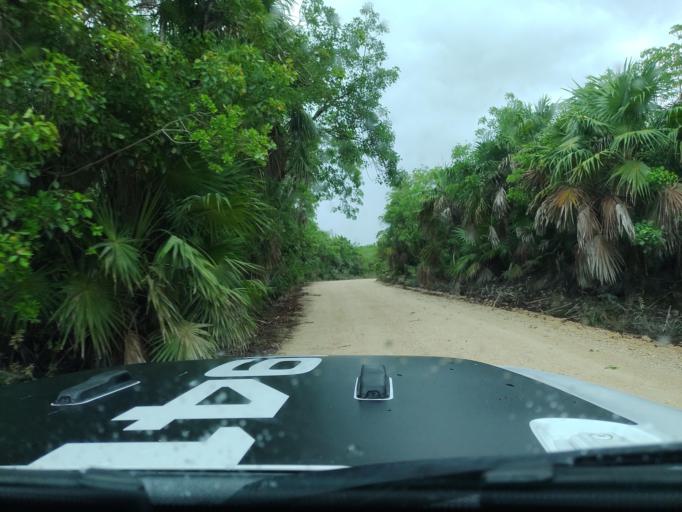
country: MX
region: Quintana Roo
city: Tulum
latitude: 20.0557
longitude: -87.4810
